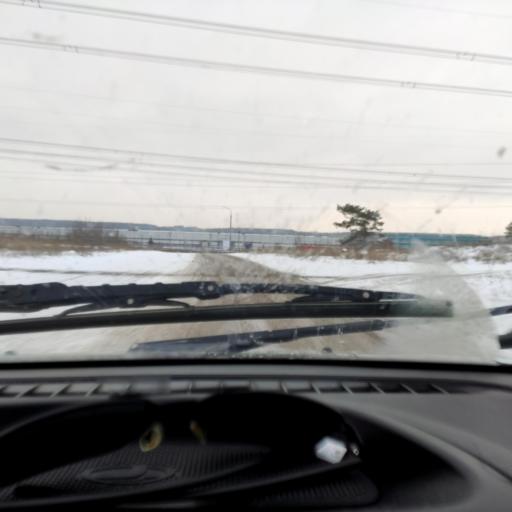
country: RU
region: Samara
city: Zhigulevsk
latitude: 53.5139
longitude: 49.5299
